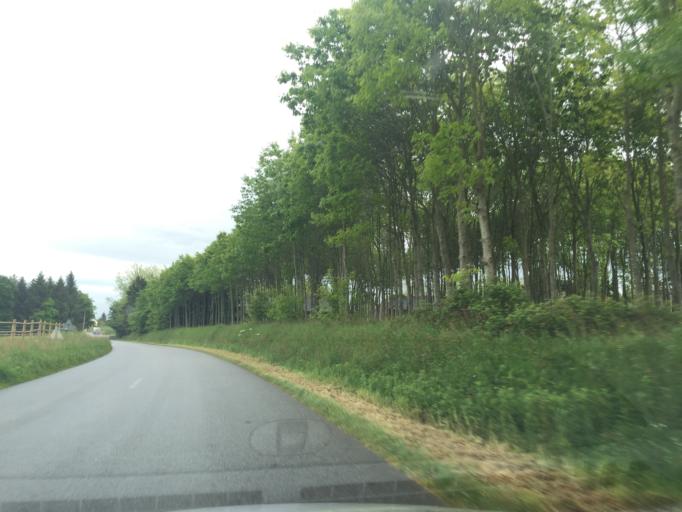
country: FR
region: Brittany
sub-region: Departement des Cotes-d'Armor
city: Crehen
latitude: 48.5535
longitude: -2.2382
